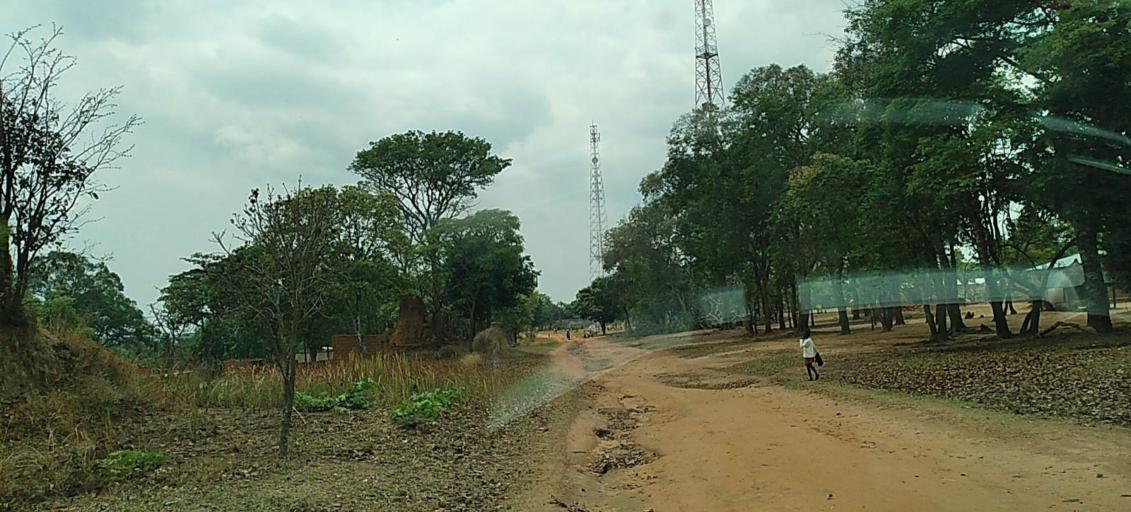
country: ZM
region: North-Western
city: Mwinilunga
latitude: -11.5219
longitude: 24.7883
